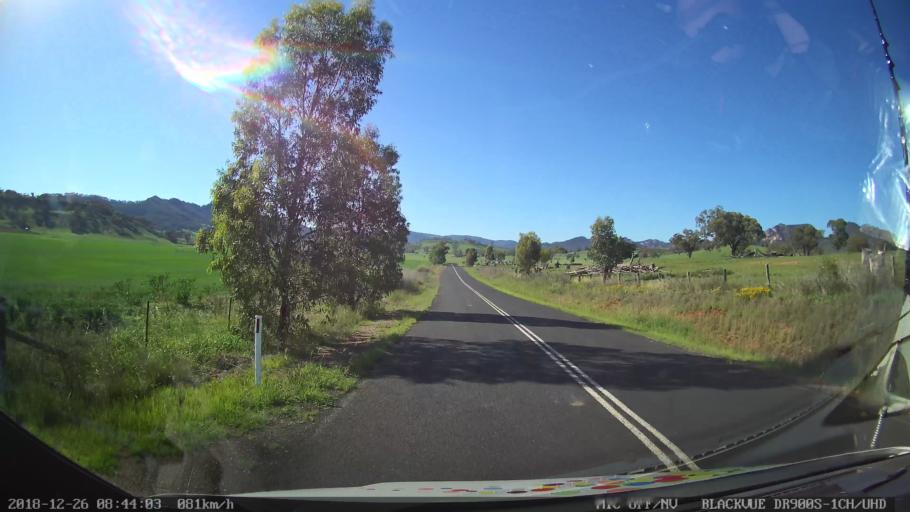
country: AU
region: New South Wales
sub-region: Mid-Western Regional
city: Kandos
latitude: -32.5098
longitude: 150.0802
